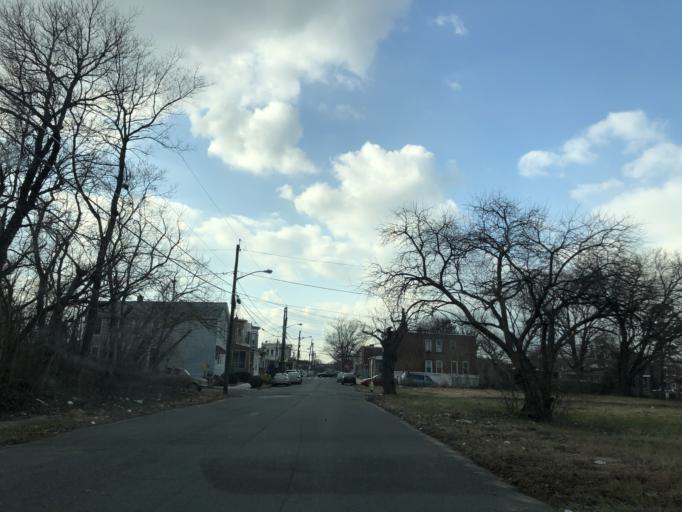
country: US
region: New Jersey
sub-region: Camden County
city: Wood-Lynne
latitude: 39.9181
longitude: -75.1090
